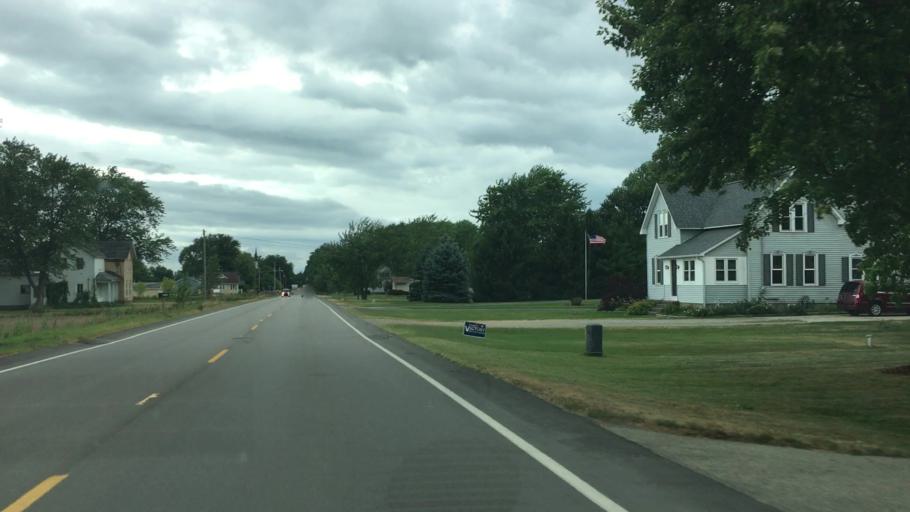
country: US
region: Michigan
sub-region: Ottawa County
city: Zeeland
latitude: 42.7828
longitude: -85.9330
